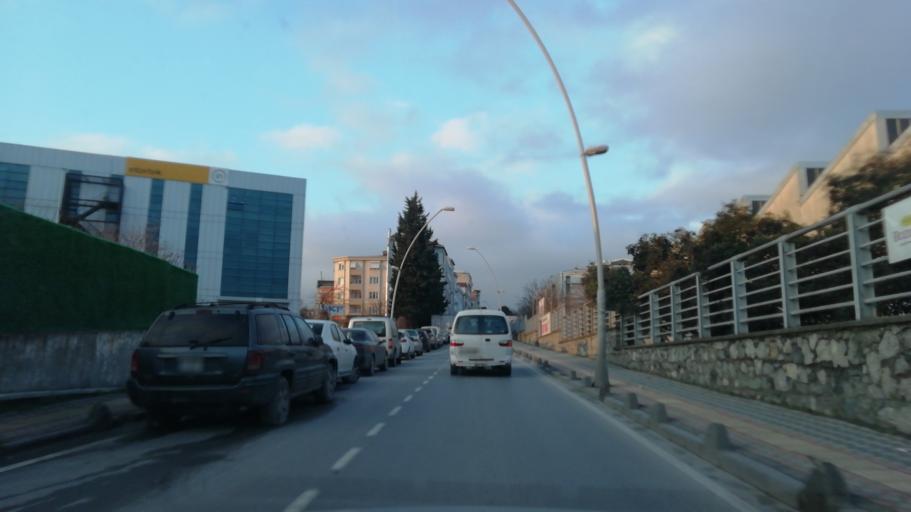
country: TR
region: Istanbul
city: Bahcelievler
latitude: 41.0058
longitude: 28.8217
